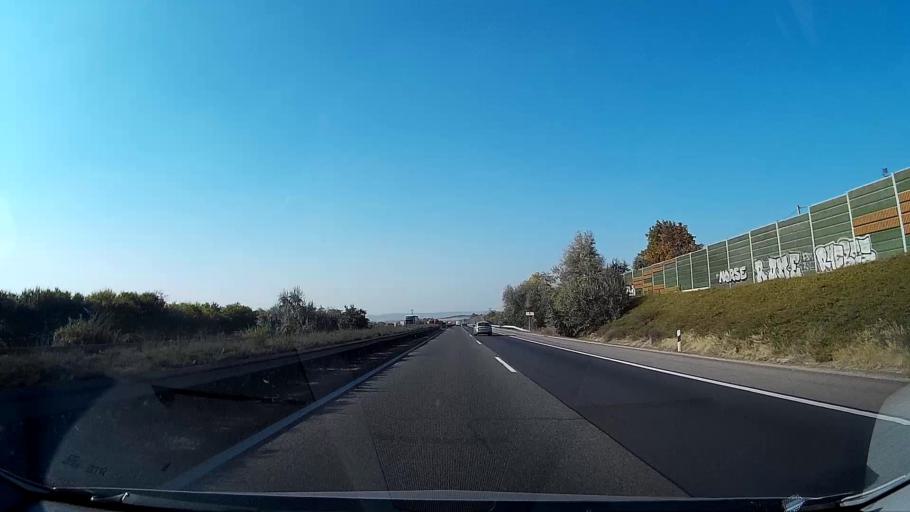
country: HU
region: Pest
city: Biatorbagy
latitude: 47.4822
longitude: 18.8401
